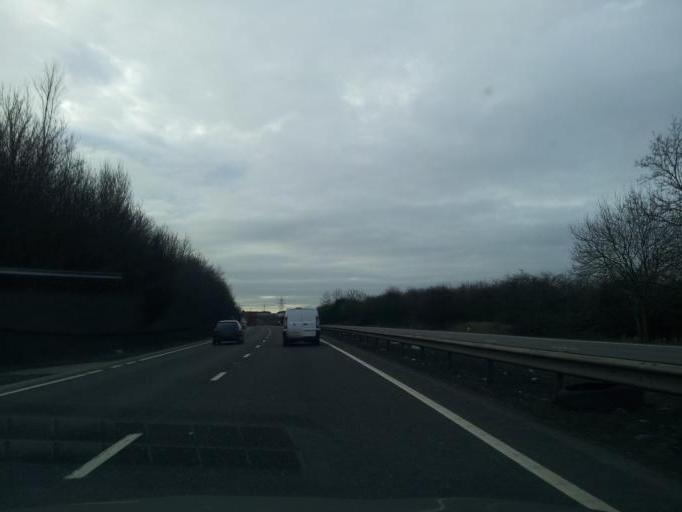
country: GB
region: England
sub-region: Lincolnshire
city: Great Gonerby
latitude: 52.9368
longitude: -0.6851
